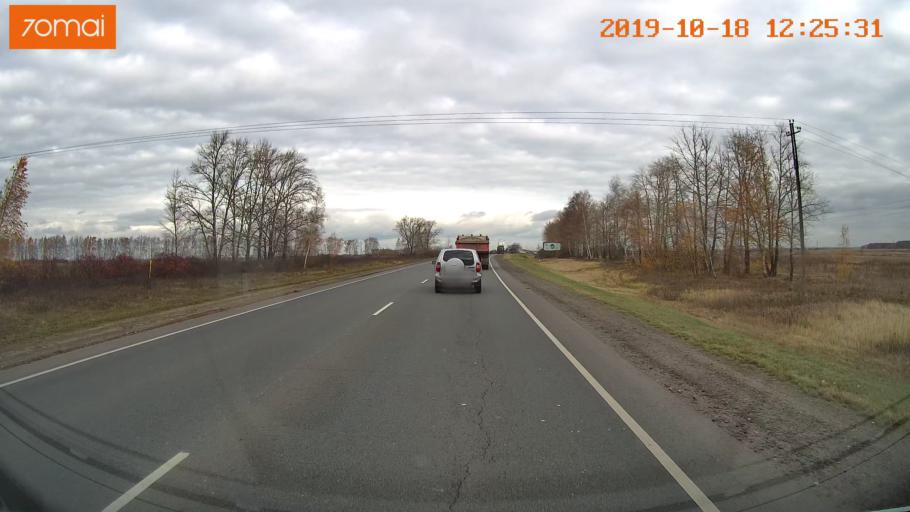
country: RU
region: Rjazan
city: Rybnoye
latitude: 54.5508
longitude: 39.5215
